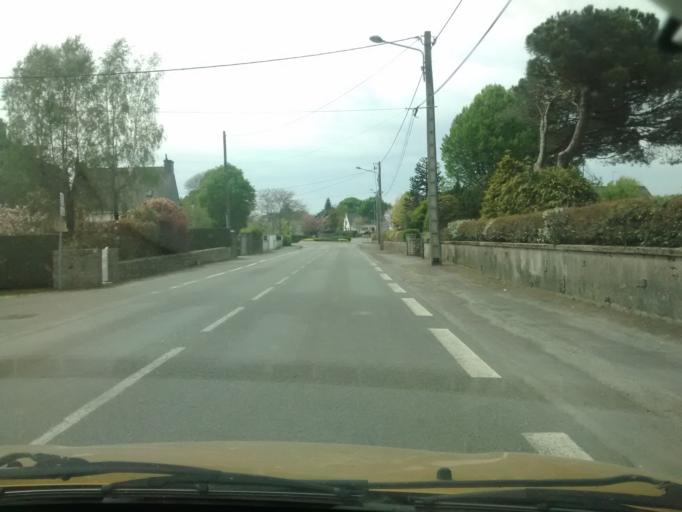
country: FR
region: Brittany
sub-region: Departement du Morbihan
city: Questembert
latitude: 47.6647
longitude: -2.4583
